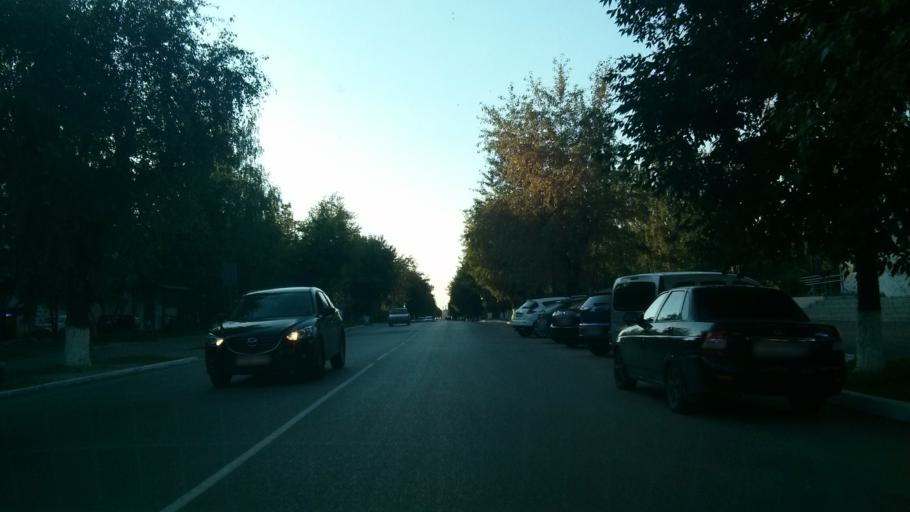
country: RU
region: Vladimir
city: Murom
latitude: 55.5684
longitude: 42.0555
